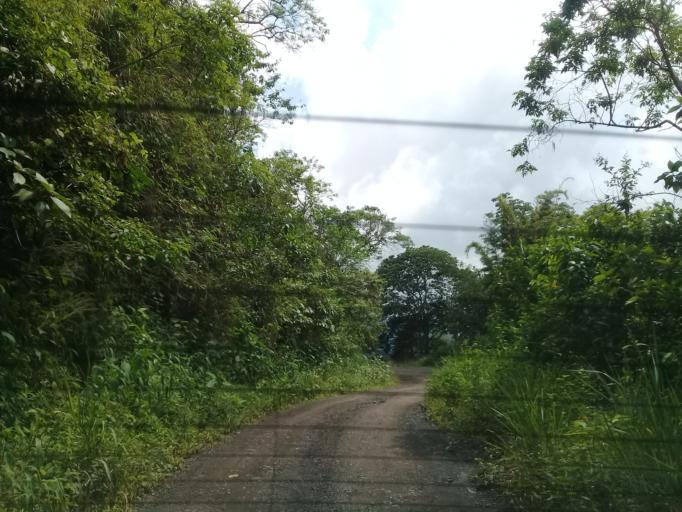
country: CO
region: Cundinamarca
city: Quipile
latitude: 4.7152
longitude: -74.5463
